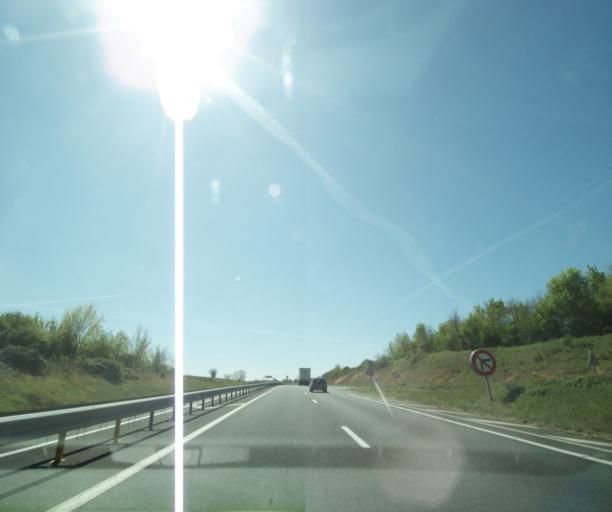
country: FR
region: Centre
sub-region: Departement de l'Indre
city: Argenton-sur-Creuse
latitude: 46.5470
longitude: 1.5062
